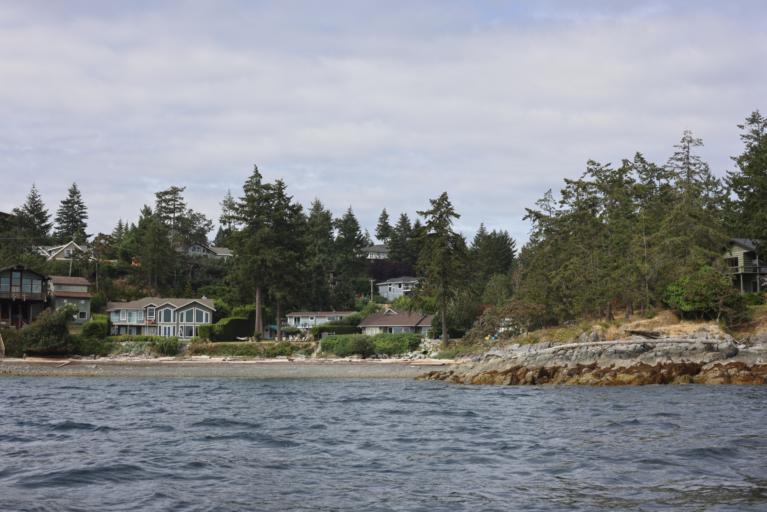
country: CA
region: British Columbia
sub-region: Regional District of Nanaimo
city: Parksville
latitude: 49.2837
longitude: -124.1285
